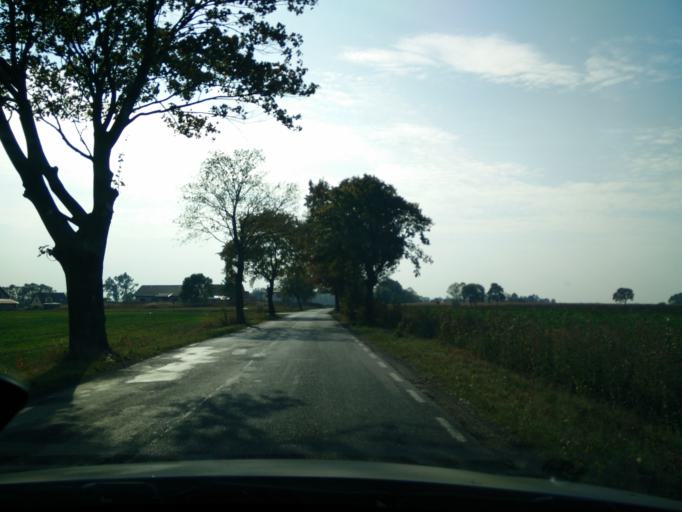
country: PL
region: Greater Poland Voivodeship
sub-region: Powiat sredzki
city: Dominowo
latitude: 52.2706
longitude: 17.3158
